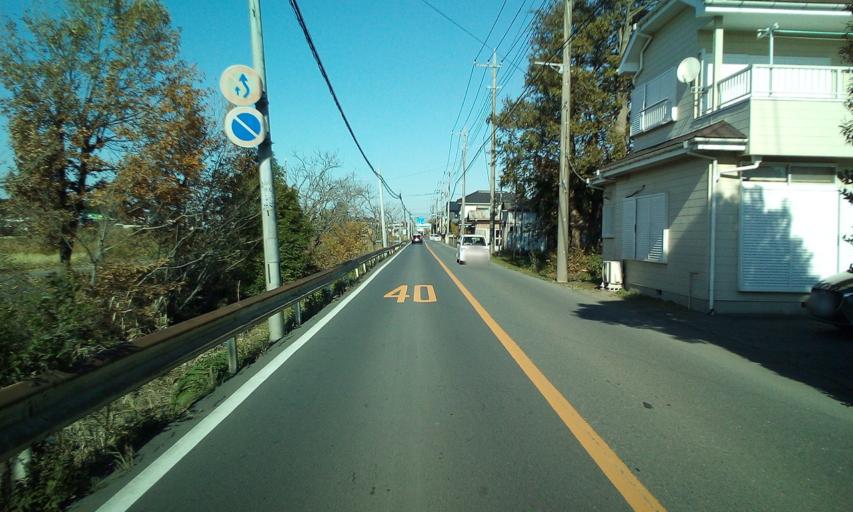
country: JP
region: Saitama
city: Kasukabe
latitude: 35.9863
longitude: 139.7967
